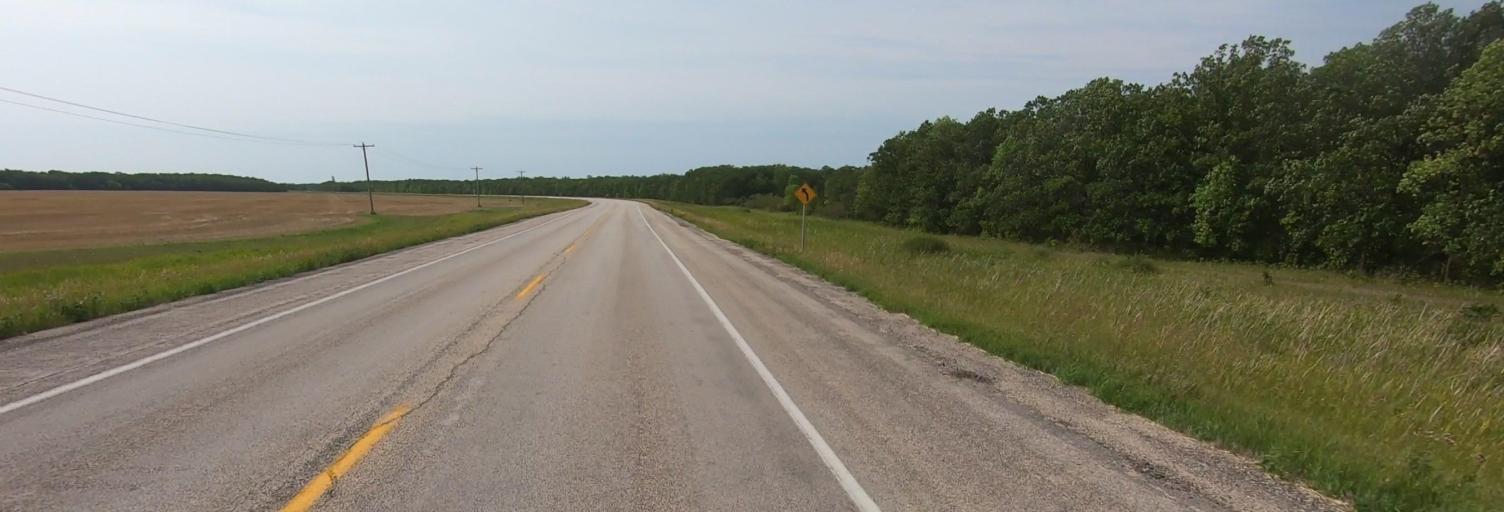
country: CA
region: Manitoba
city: Niverville
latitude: 49.6009
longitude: -97.1329
